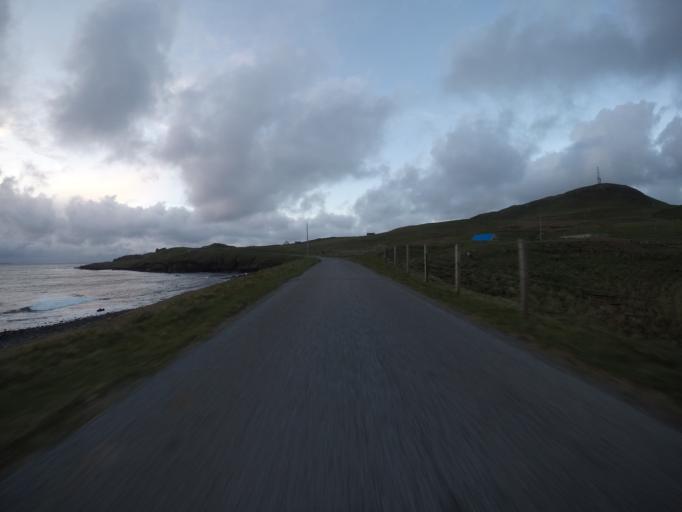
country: GB
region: Scotland
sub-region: Highland
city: Portree
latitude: 57.6786
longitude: -6.3454
